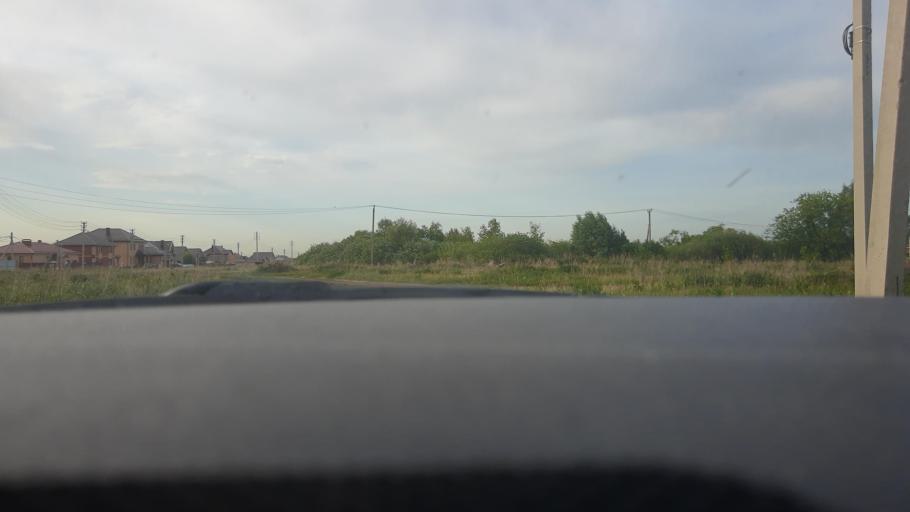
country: RU
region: Bashkortostan
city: Kabakovo
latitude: 54.6062
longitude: 56.1225
